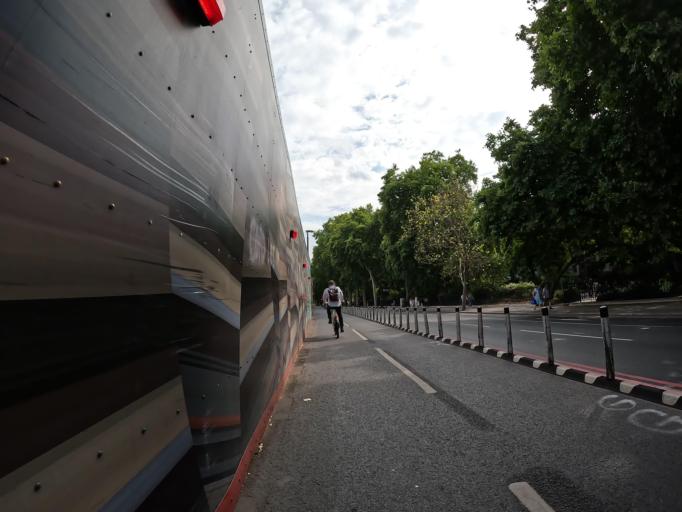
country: GB
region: England
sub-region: Greater London
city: Catford
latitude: 51.4531
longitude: -0.0072
